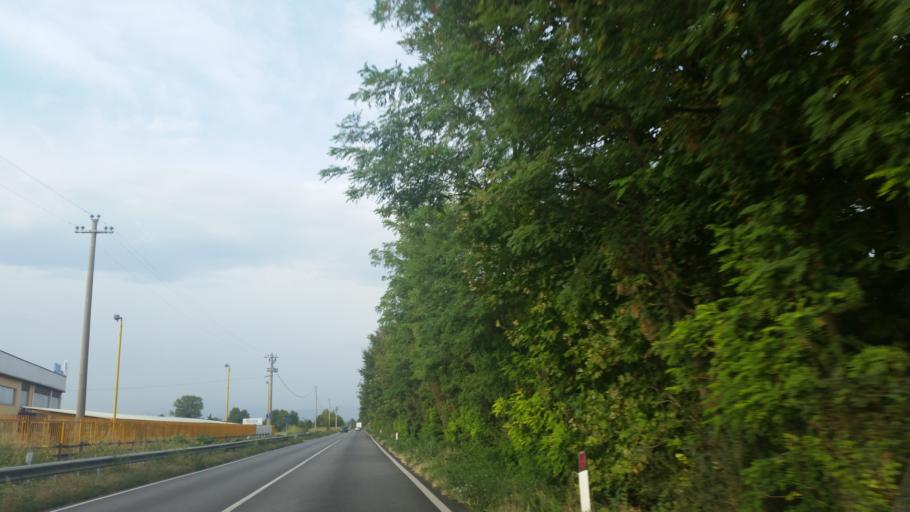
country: IT
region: Lombardy
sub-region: Provincia di Brescia
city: Dello
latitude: 45.4054
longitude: 10.0739
